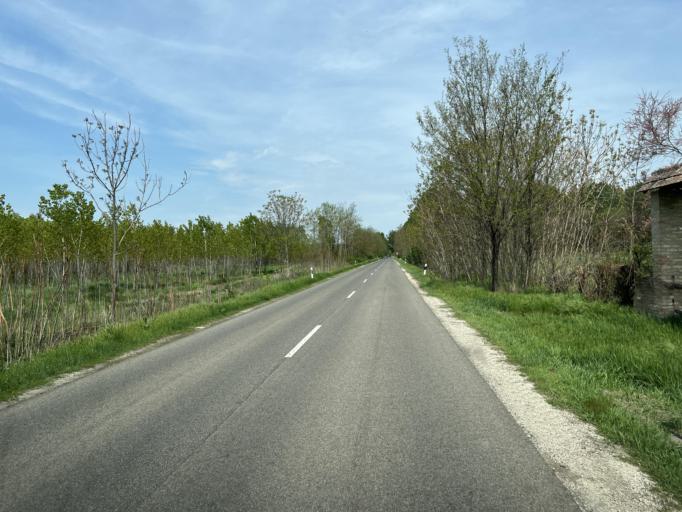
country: HU
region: Pest
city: Ujszilvas
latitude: 47.2498
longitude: 19.9459
